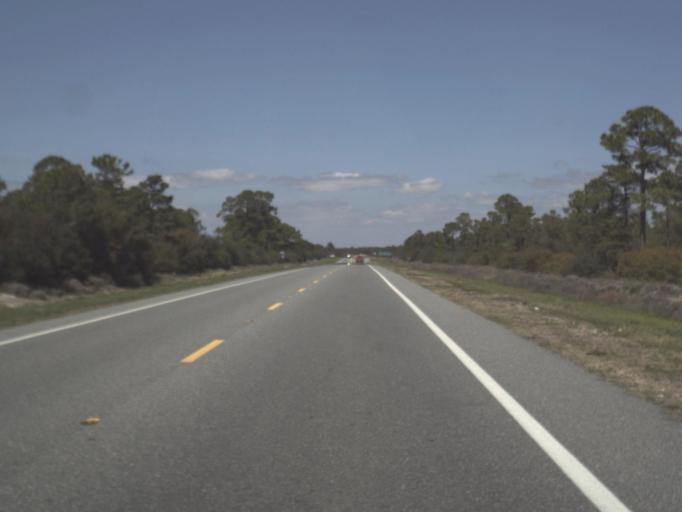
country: US
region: Florida
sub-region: Gulf County
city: Port Saint Joe
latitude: 29.8567
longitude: -85.3357
